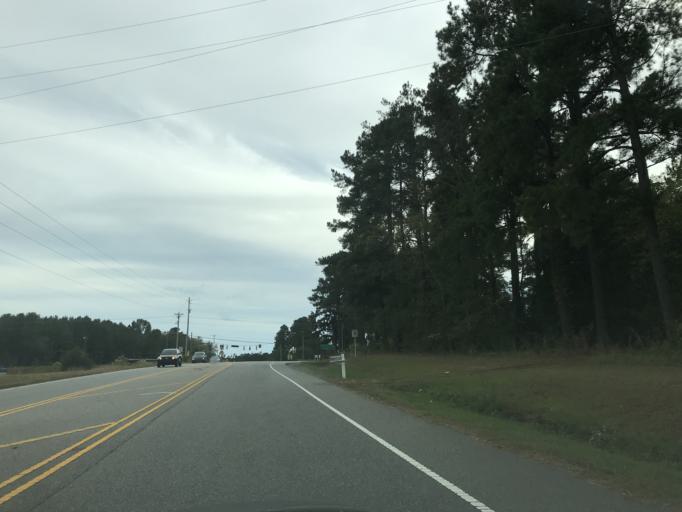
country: US
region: North Carolina
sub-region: Wake County
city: Rolesville
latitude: 35.8978
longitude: -78.5068
